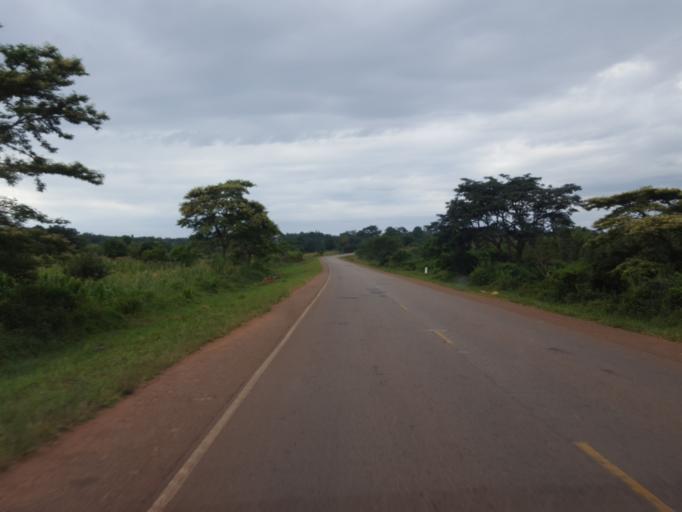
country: UG
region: Central Region
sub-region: Kiboga District
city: Kiboga
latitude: 1.0194
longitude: 31.6875
